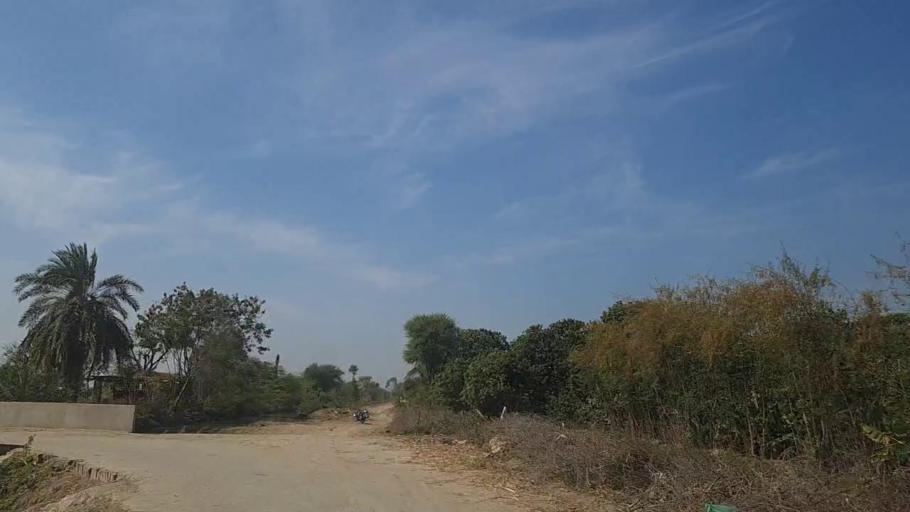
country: PK
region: Sindh
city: Mirpur Khas
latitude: 25.4682
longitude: 68.9625
